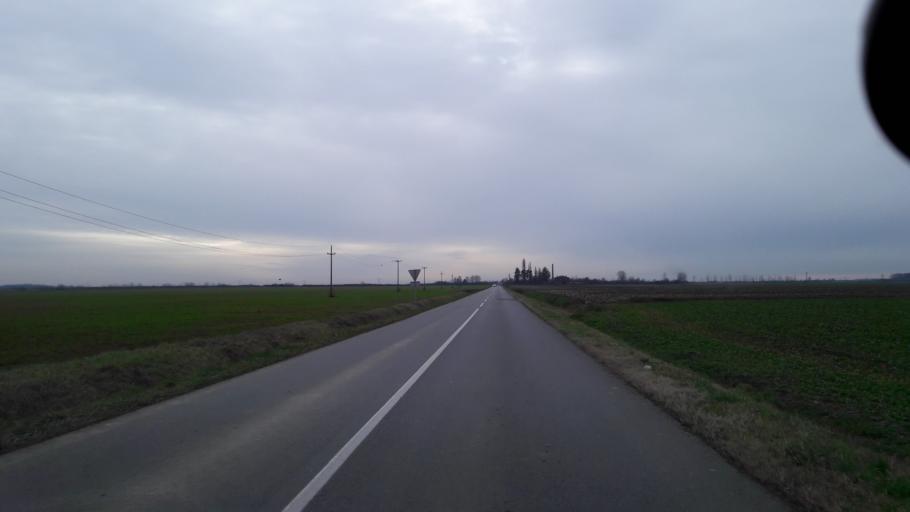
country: HR
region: Osjecko-Baranjska
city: Ovcara
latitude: 45.4884
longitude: 18.5500
